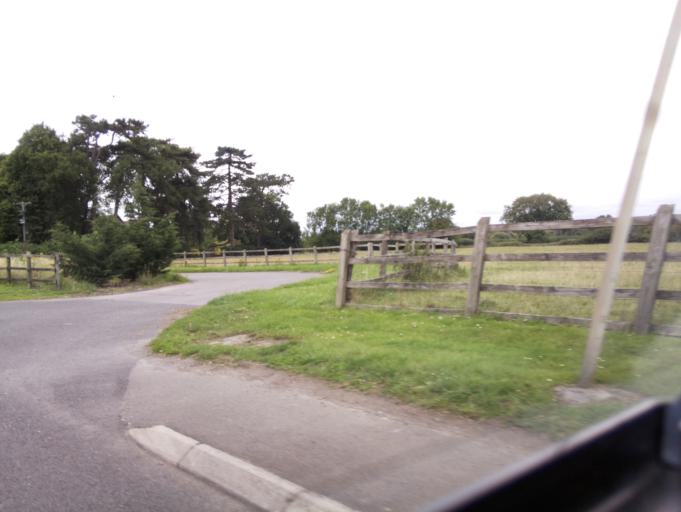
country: GB
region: England
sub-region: North Somerset
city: Kenn
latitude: 51.4183
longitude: -2.8453
